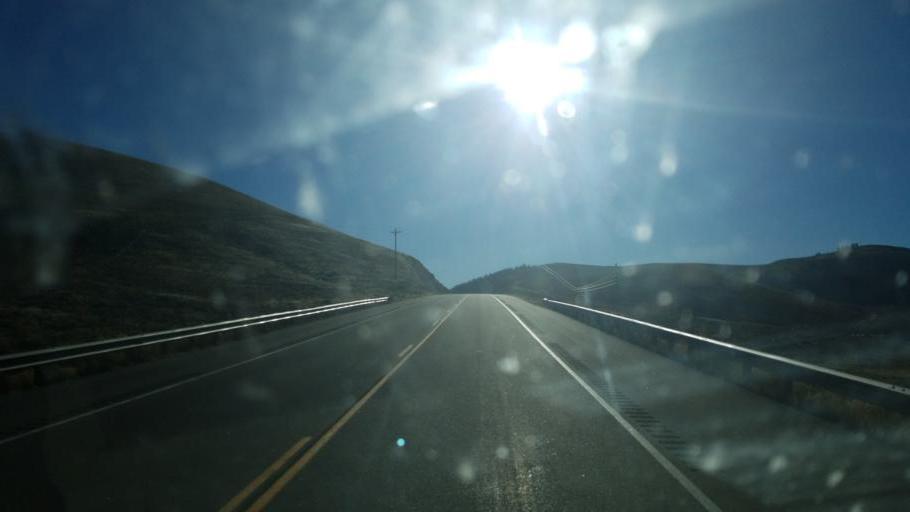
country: US
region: Colorado
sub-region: Gunnison County
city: Gunnison
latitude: 38.5289
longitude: -106.8194
